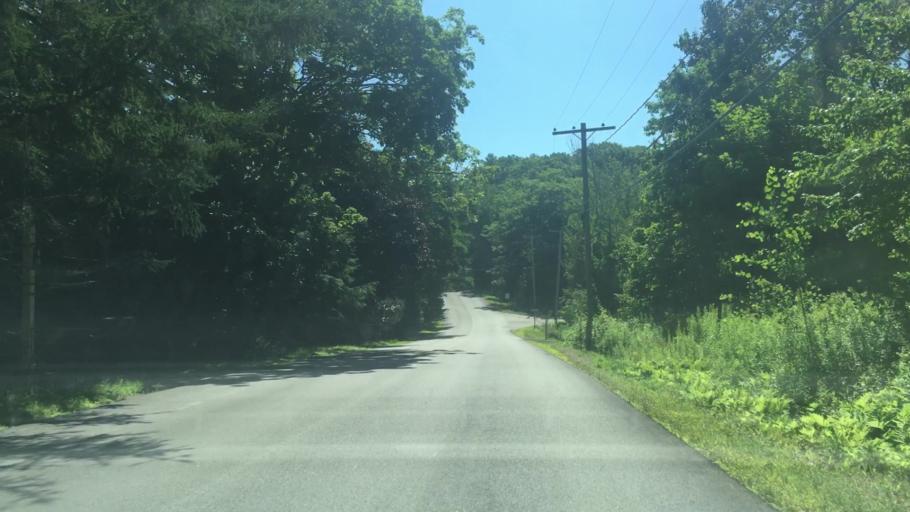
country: US
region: Maine
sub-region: Waldo County
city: Northport
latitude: 44.3816
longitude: -68.9752
